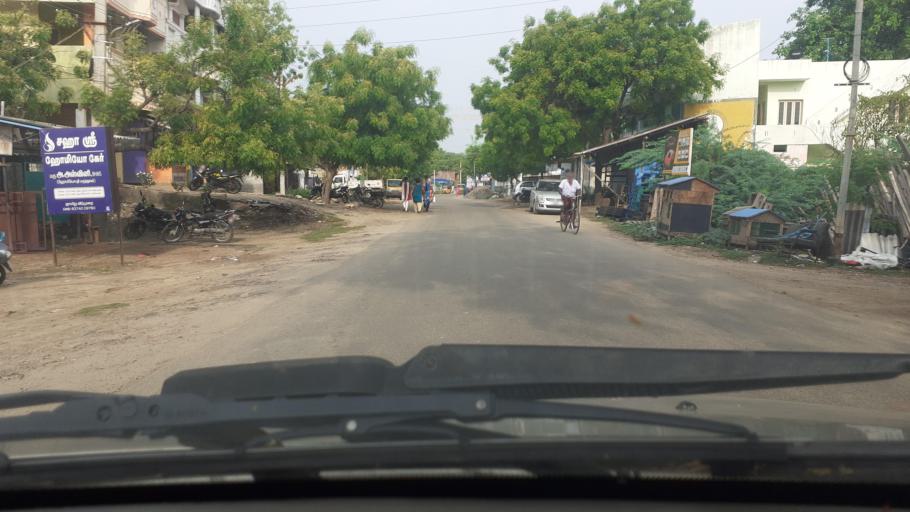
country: IN
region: Tamil Nadu
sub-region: Thoothukkudi
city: Korampallam
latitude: 8.7917
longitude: 78.1122
